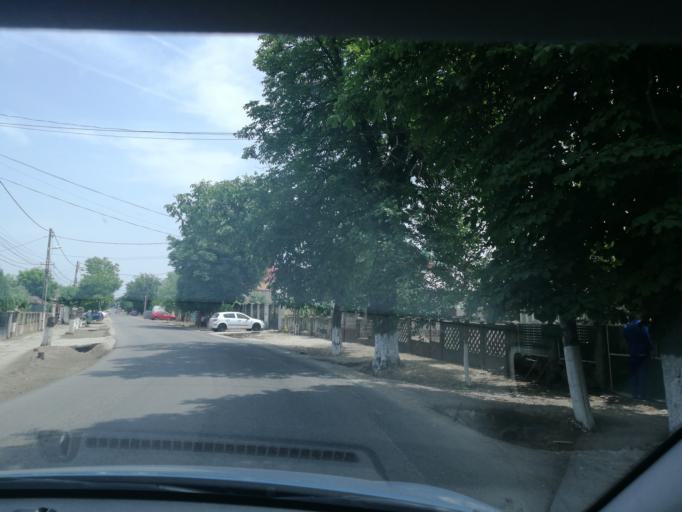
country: RO
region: Ilfov
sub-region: Comuna Jilava
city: Jilava
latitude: 44.3257
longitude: 26.0855
